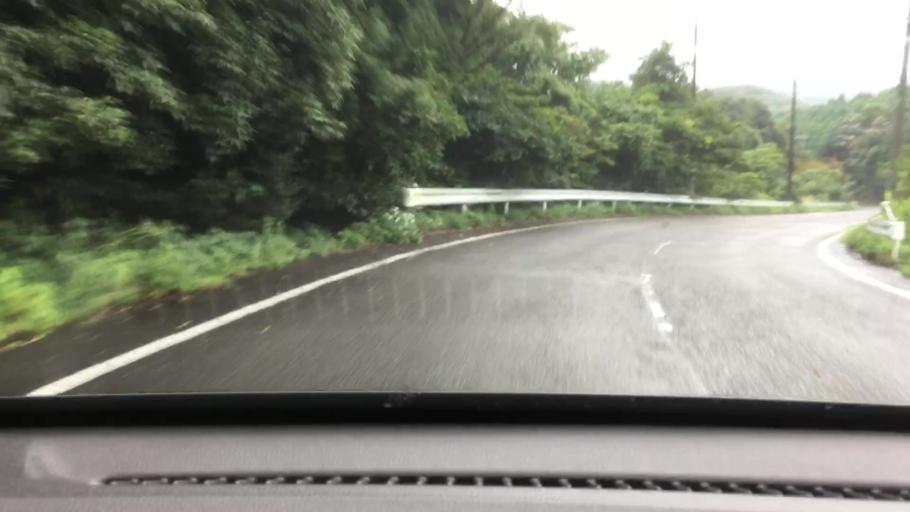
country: JP
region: Nagasaki
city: Togitsu
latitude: 32.8788
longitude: 129.7607
